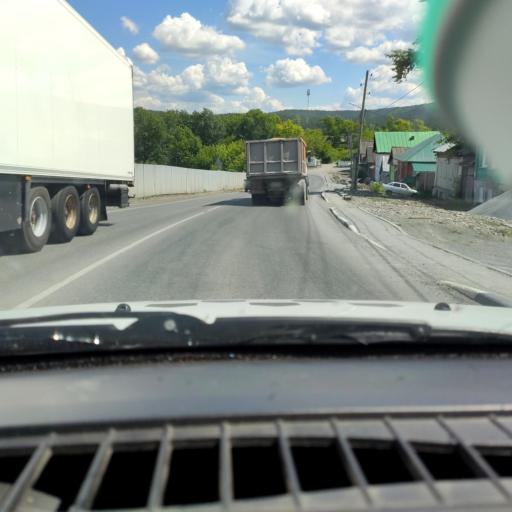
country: RU
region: Chelyabinsk
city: Satka
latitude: 55.0350
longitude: 59.0217
